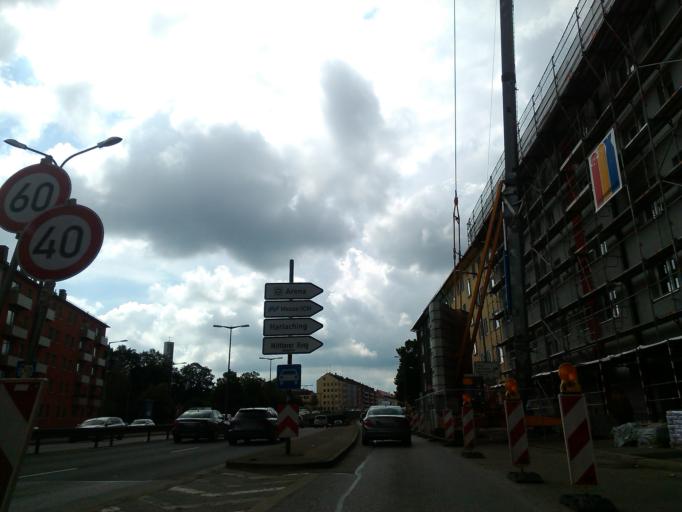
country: DE
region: Bavaria
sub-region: Upper Bavaria
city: Munich
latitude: 48.1065
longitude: 11.5804
